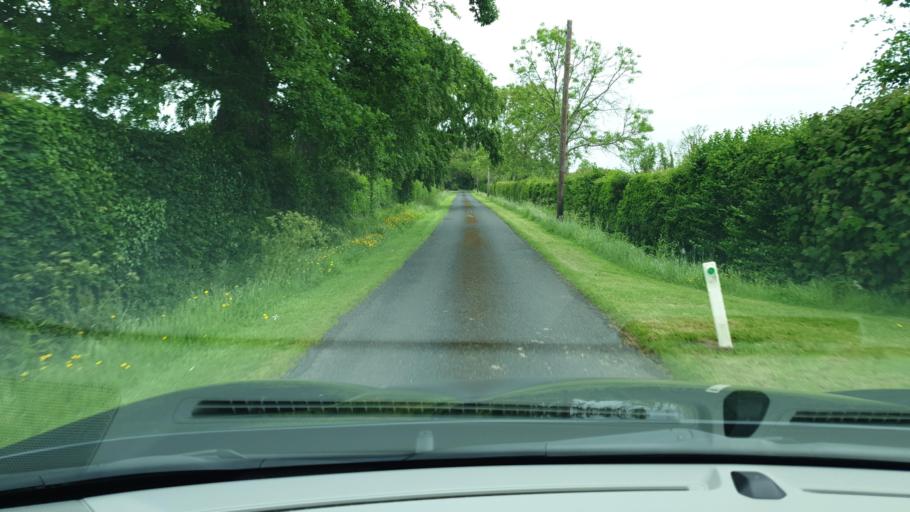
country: IE
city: Confey
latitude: 53.4178
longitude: -6.5318
